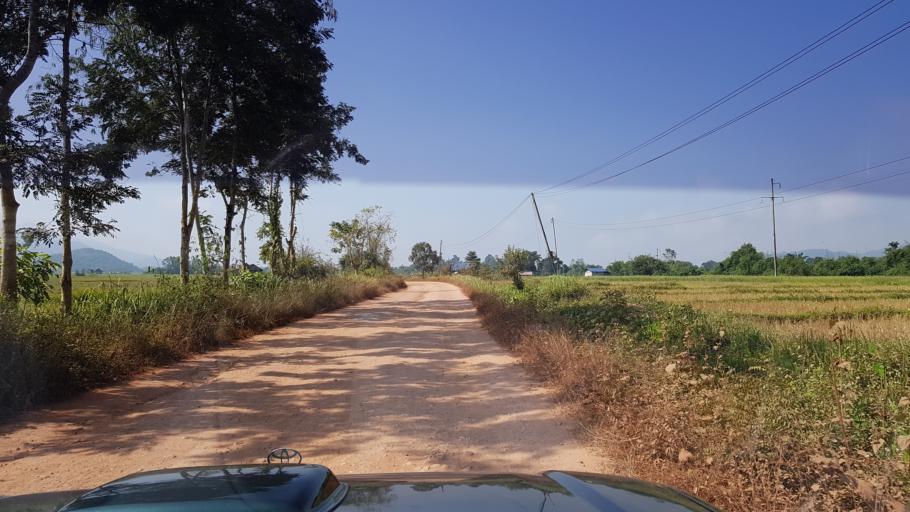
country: LA
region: Oudomxai
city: Muang Xay
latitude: 20.7189
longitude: 102.0448
